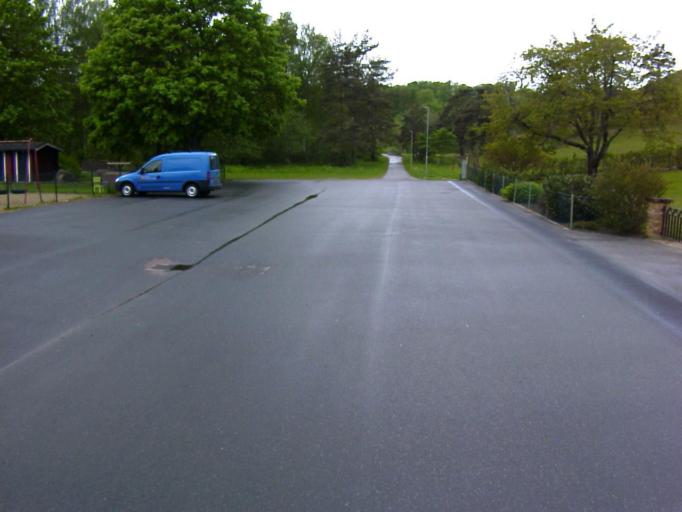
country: SE
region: Skane
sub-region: Kristianstads Kommun
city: Degeberga
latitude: 55.8318
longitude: 14.0854
